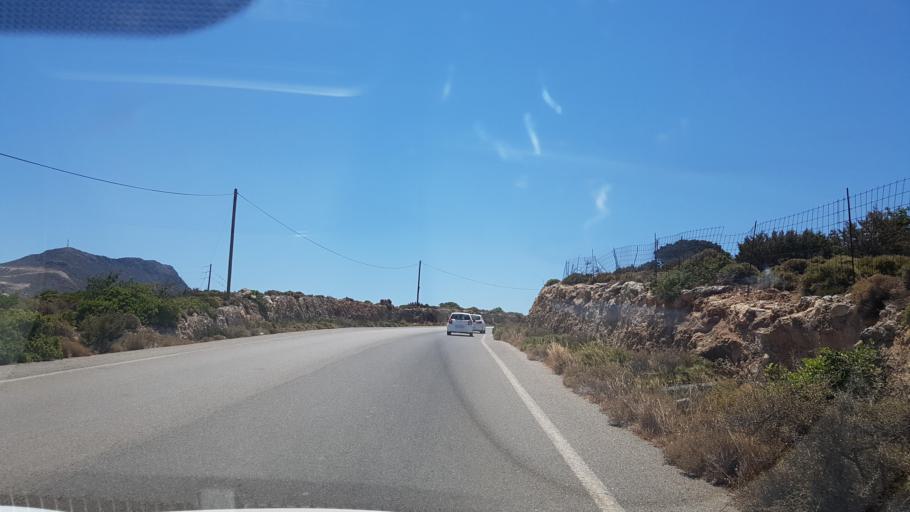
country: GR
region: Crete
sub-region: Nomos Chanias
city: Palaiochora
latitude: 35.2881
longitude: 23.5488
